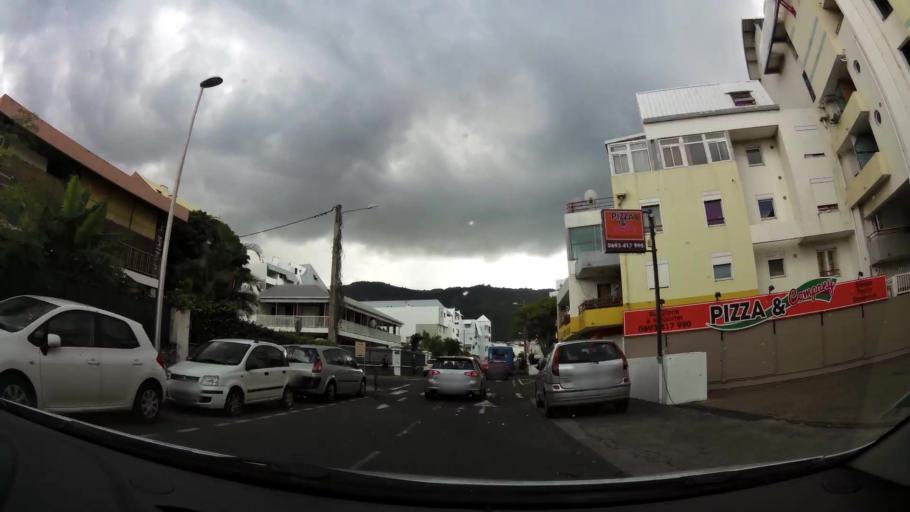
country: RE
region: Reunion
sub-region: Reunion
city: Saint-Denis
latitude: -20.8887
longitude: 55.4576
